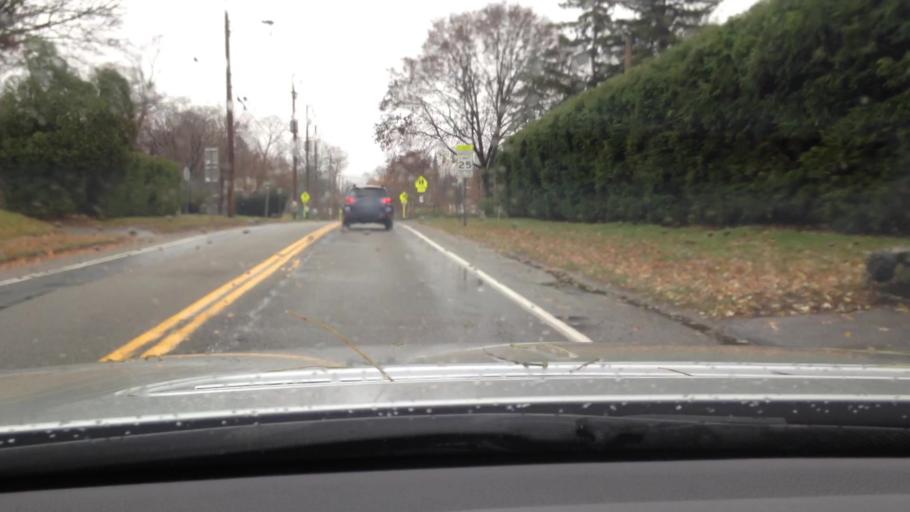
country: US
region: New York
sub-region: Putnam County
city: Cold Spring
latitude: 41.4228
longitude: -73.9590
